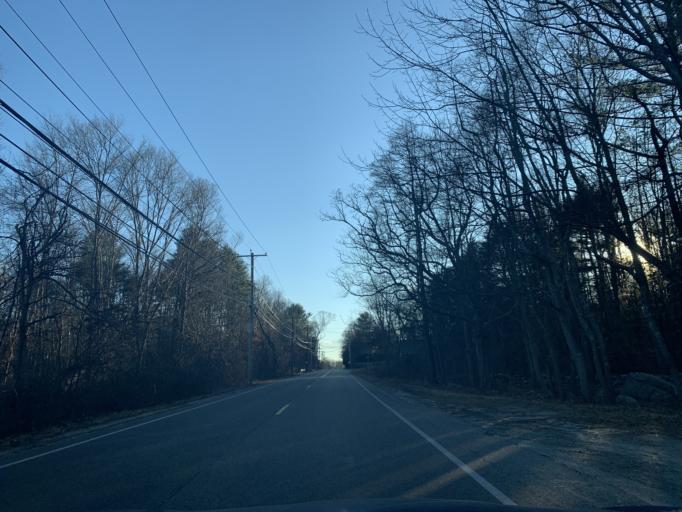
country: US
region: Massachusetts
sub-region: Bristol County
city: Rehoboth
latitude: 41.8652
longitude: -71.2358
